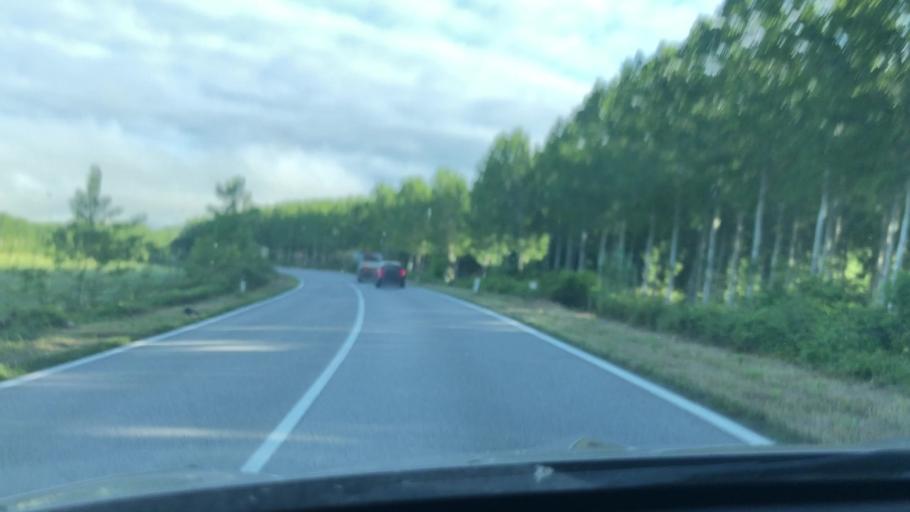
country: IT
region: Tuscany
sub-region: Province of Pisa
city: Forcoli
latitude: 43.6030
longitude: 10.6938
